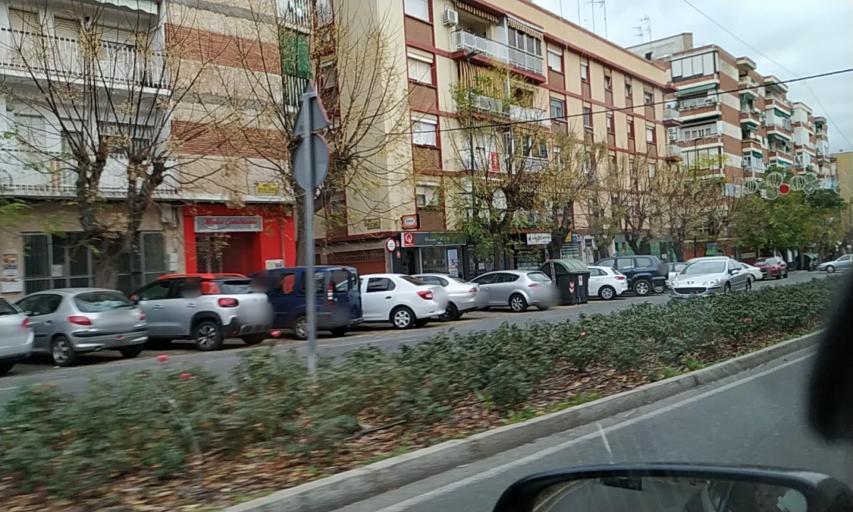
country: ES
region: Extremadura
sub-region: Provincia de Badajoz
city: Badajoz
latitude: 38.8884
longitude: -6.9825
